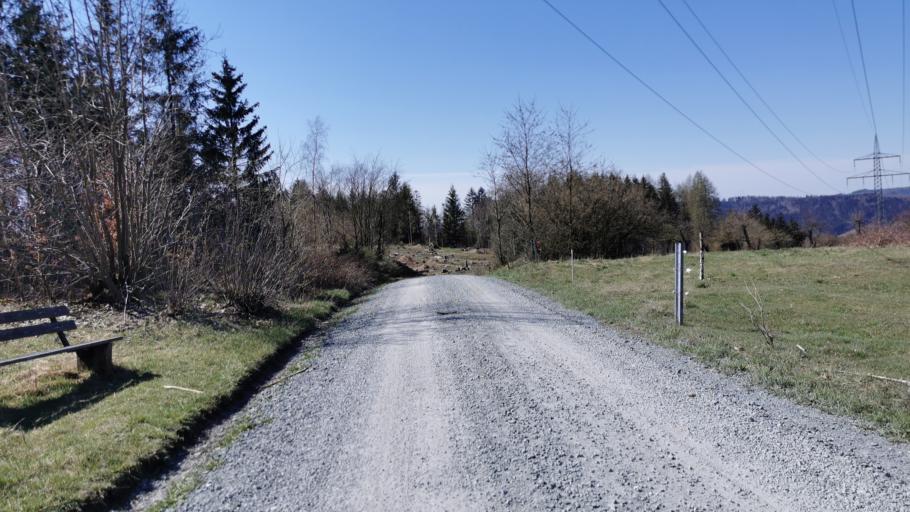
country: DE
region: Bavaria
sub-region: Upper Franconia
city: Pressig
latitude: 50.3781
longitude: 11.3252
